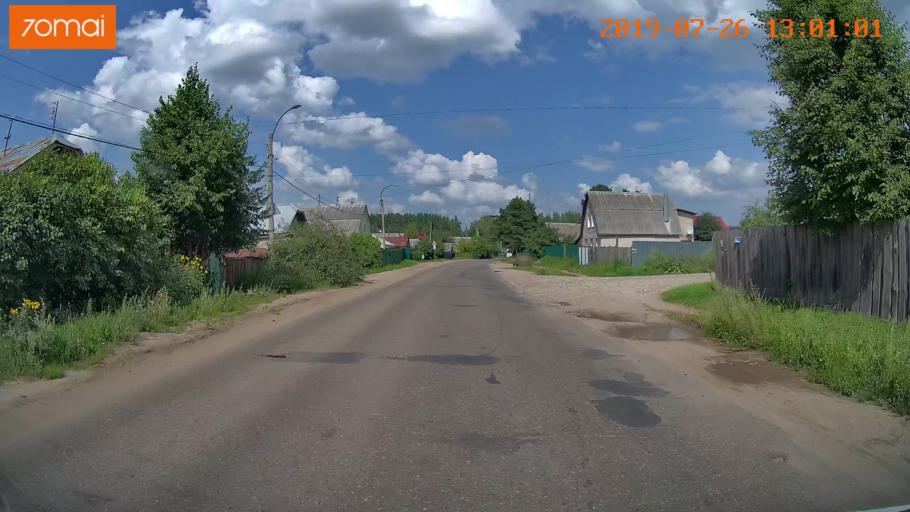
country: RU
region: Ivanovo
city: Bogorodskoye
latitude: 57.0366
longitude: 41.0126
